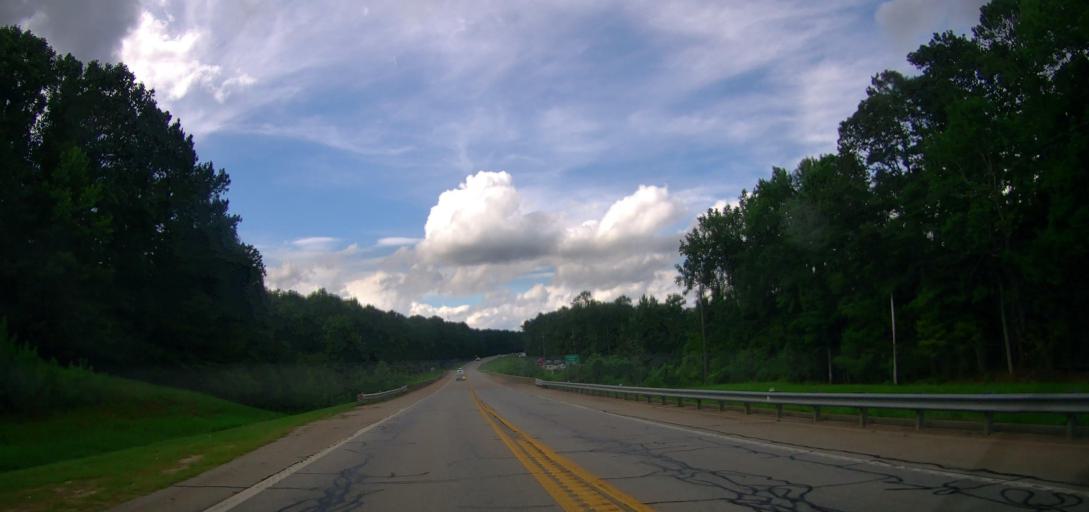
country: US
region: Georgia
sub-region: Harris County
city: Hamilton
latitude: 32.7075
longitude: -84.8693
